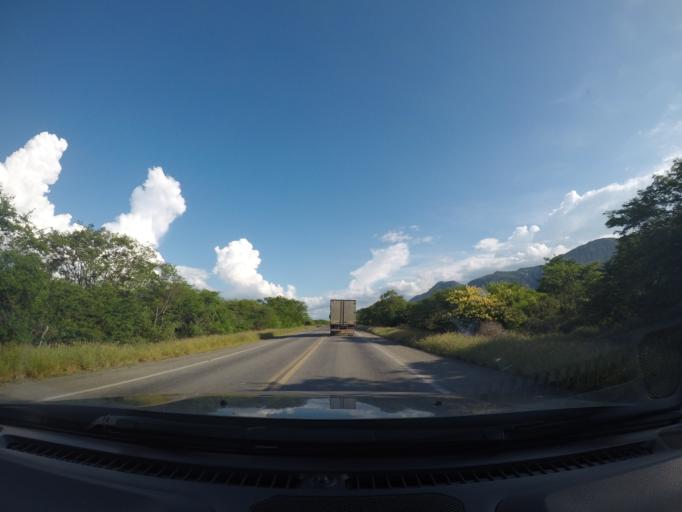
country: BR
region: Bahia
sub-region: Oliveira Dos Brejinhos
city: Oliveira dos Brejinhos
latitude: -12.0455
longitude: -42.9716
